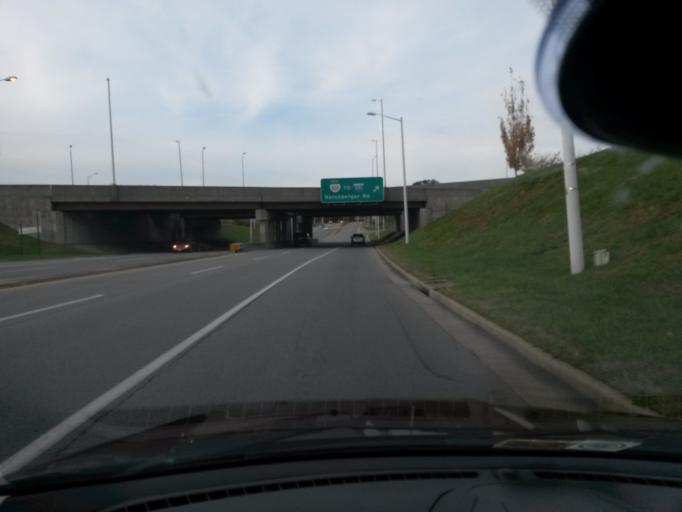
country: US
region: Virginia
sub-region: Roanoke County
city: Hollins
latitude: 37.3126
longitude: -79.9660
